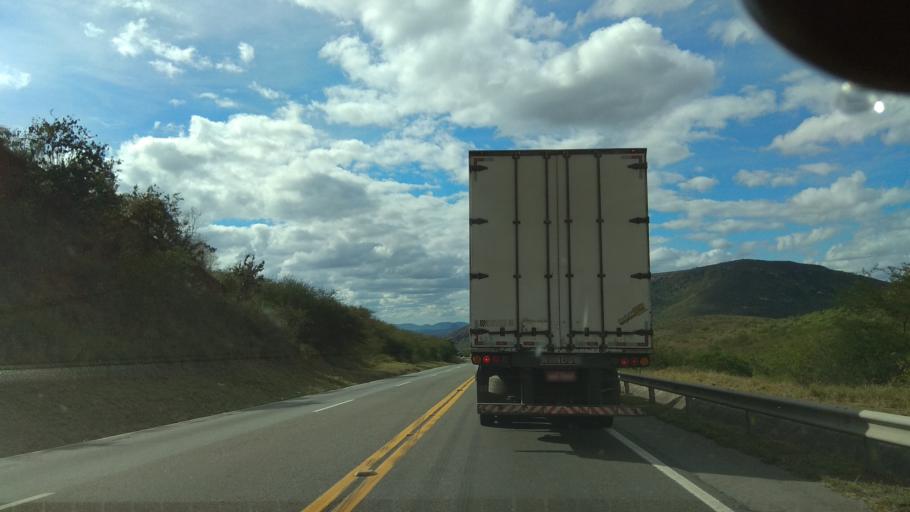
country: BR
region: Bahia
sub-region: Amargosa
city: Amargosa
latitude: -12.8923
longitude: -39.8595
